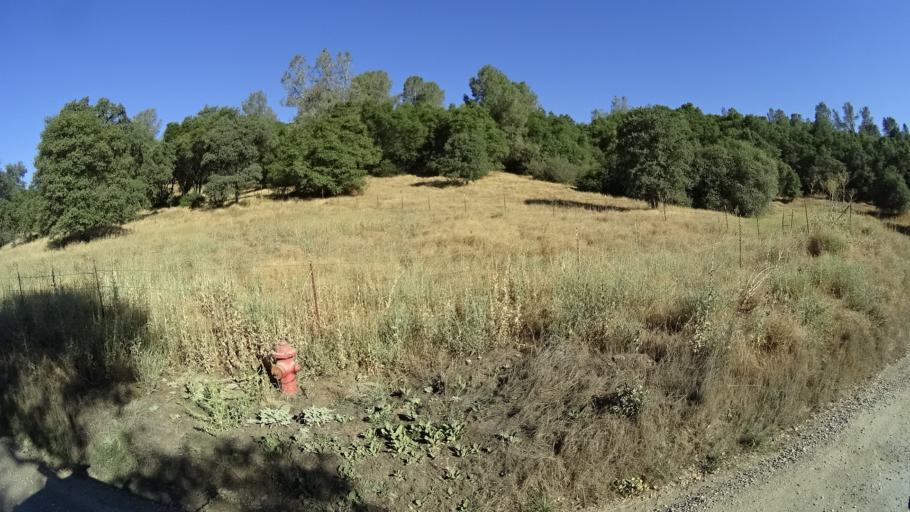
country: US
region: California
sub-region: Calaveras County
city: Angels Camp
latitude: 38.0625
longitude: -120.5004
